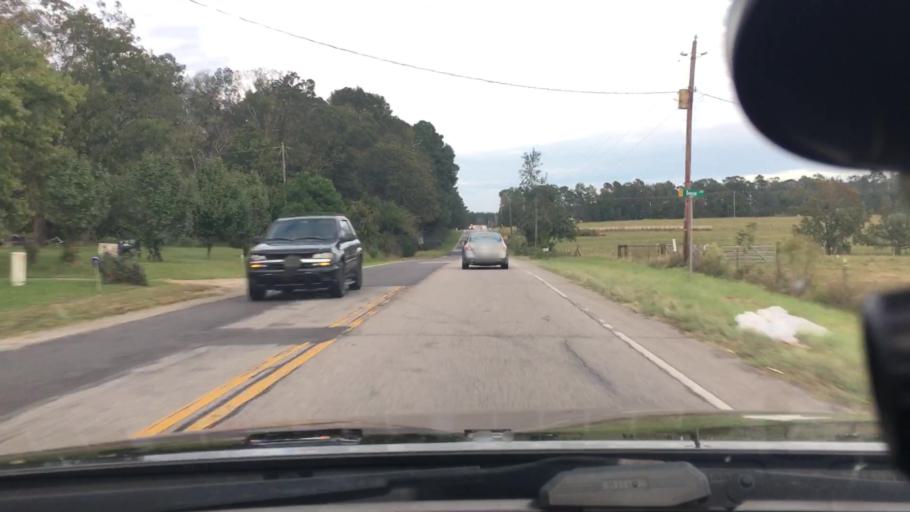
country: US
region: North Carolina
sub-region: Moore County
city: Carthage
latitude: 35.3593
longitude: -79.3296
